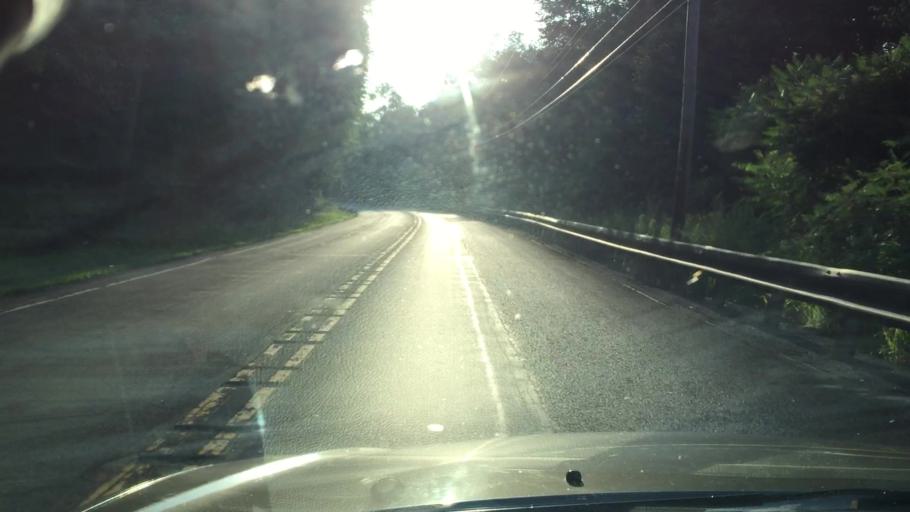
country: US
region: Pennsylvania
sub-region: Carbon County
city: Jim Thorpe
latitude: 40.8725
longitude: -75.7625
